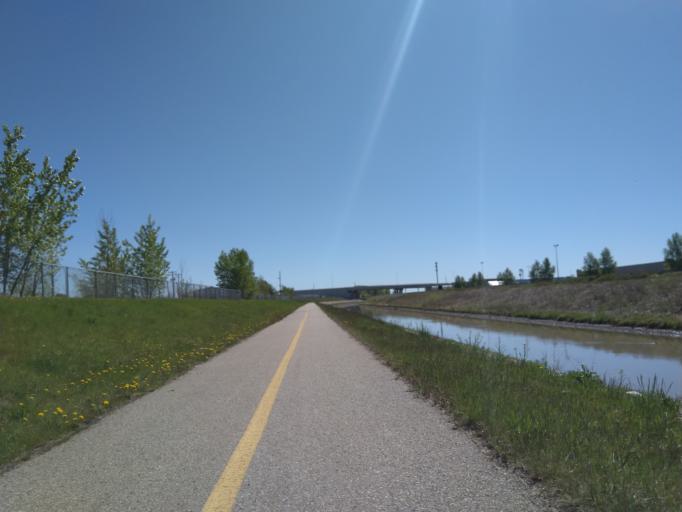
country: CA
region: Alberta
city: Calgary
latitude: 50.9647
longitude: -113.9670
